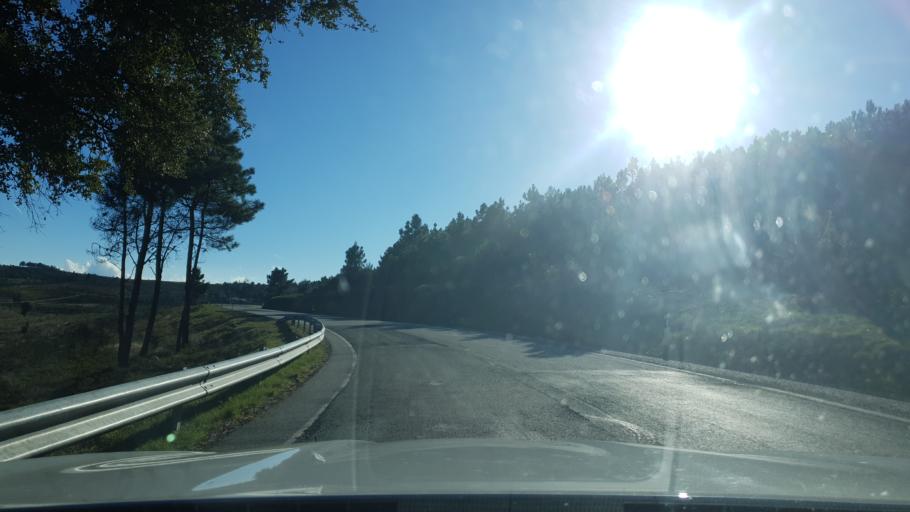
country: PT
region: Braganca
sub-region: Freixo de Espada A Cinta
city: Freixo de Espada a Cinta
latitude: 41.1665
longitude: -6.7967
